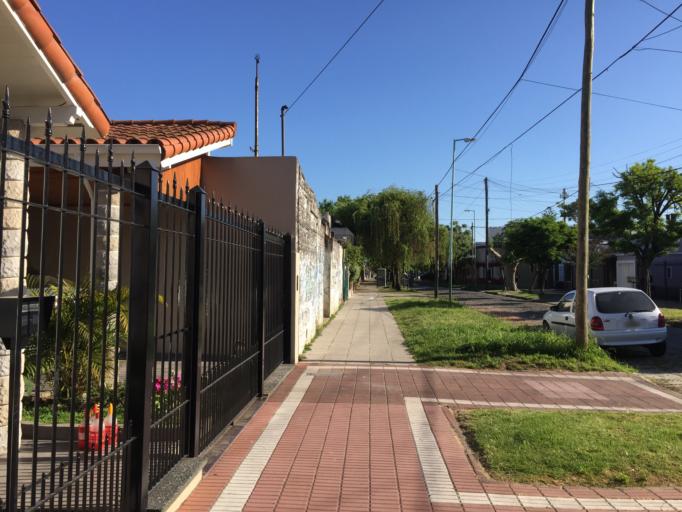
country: AR
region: Buenos Aires
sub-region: Partido de Lomas de Zamora
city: Lomas de Zamora
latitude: -34.7388
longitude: -58.3879
